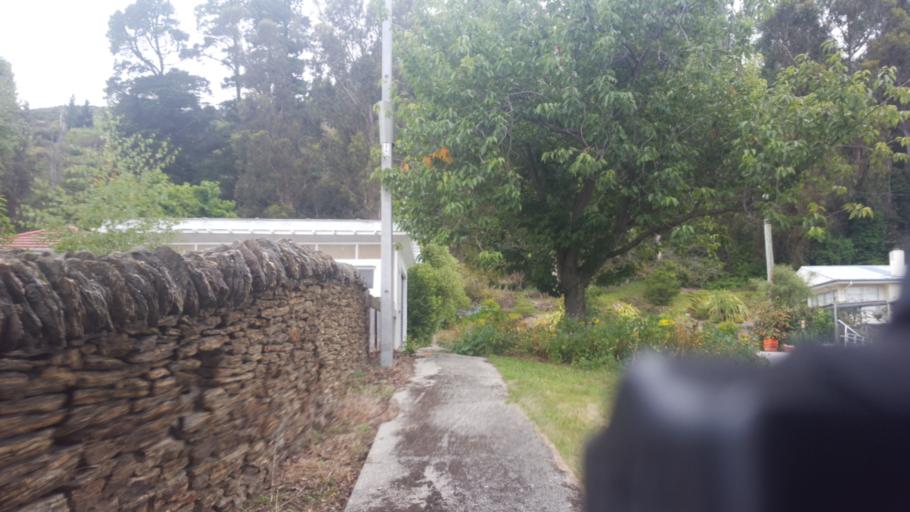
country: NZ
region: Otago
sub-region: Queenstown-Lakes District
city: Kingston
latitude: -45.5391
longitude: 169.3114
